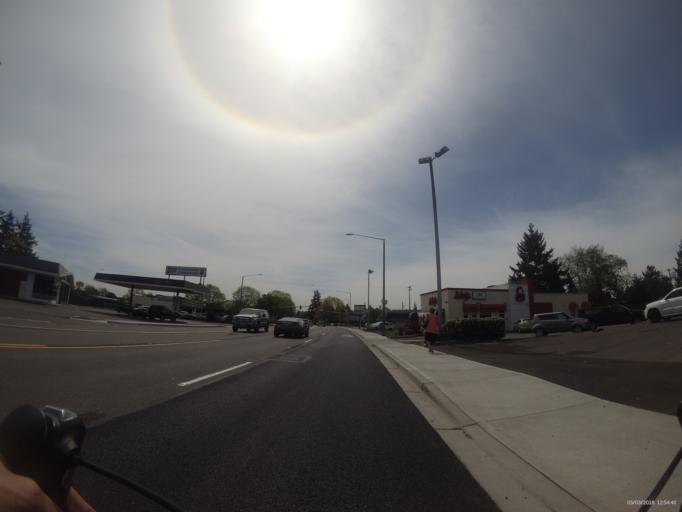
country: US
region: Washington
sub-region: Pierce County
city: Lakewood
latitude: 47.1678
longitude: -122.5206
